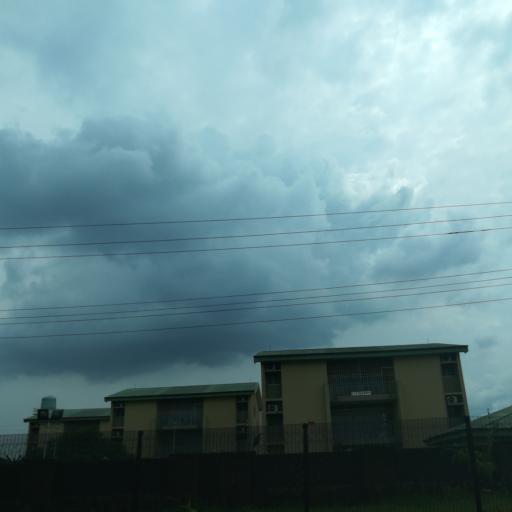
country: NG
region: Rivers
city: Port Harcourt
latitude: 4.8281
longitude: 7.0021
